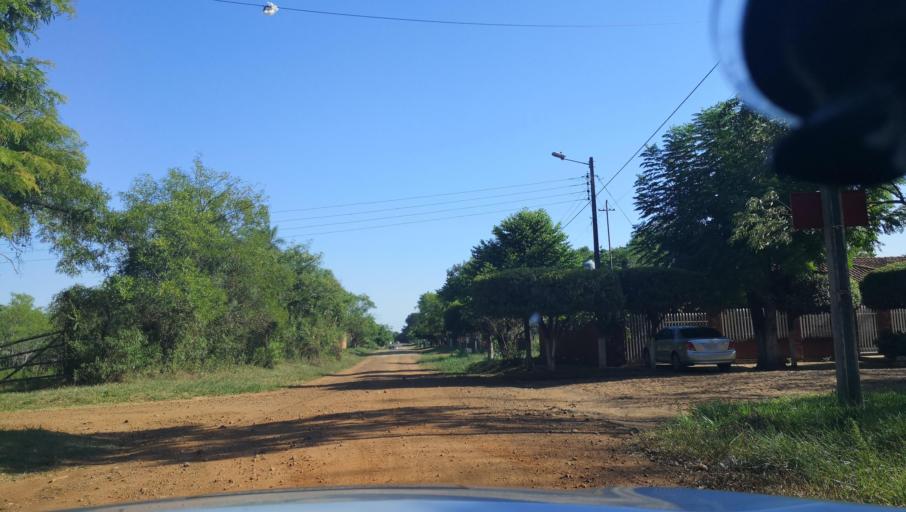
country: PY
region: Itapua
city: Carmen del Parana
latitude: -27.1667
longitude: -56.2372
